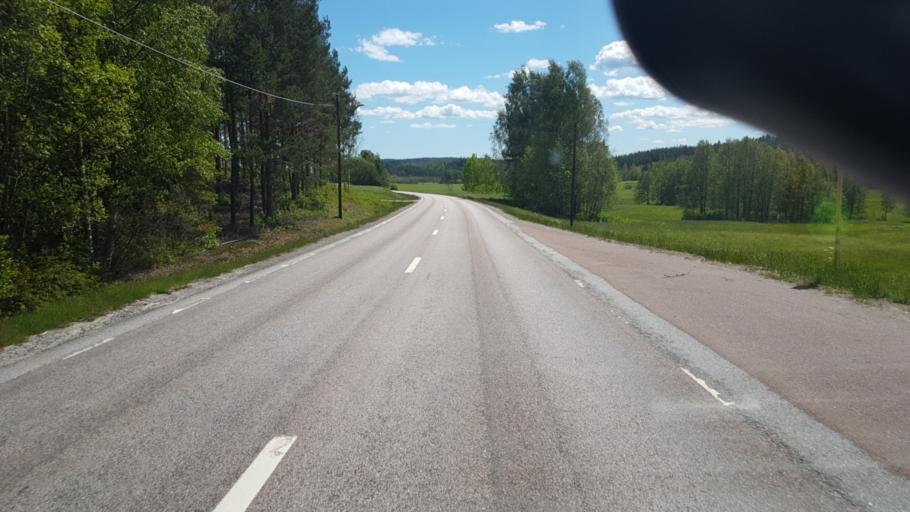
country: SE
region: Vaermland
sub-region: Arvika Kommun
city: Arvika
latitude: 59.6395
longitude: 12.7871
